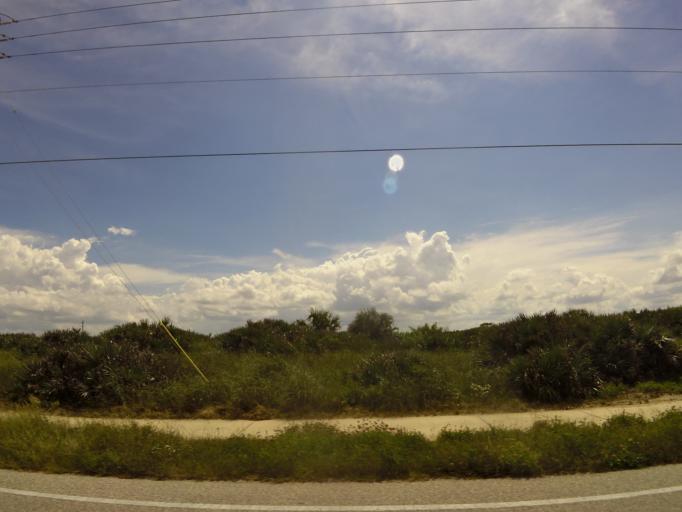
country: US
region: Florida
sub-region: Flagler County
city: Flagler Beach
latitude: 29.4195
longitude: -81.0991
